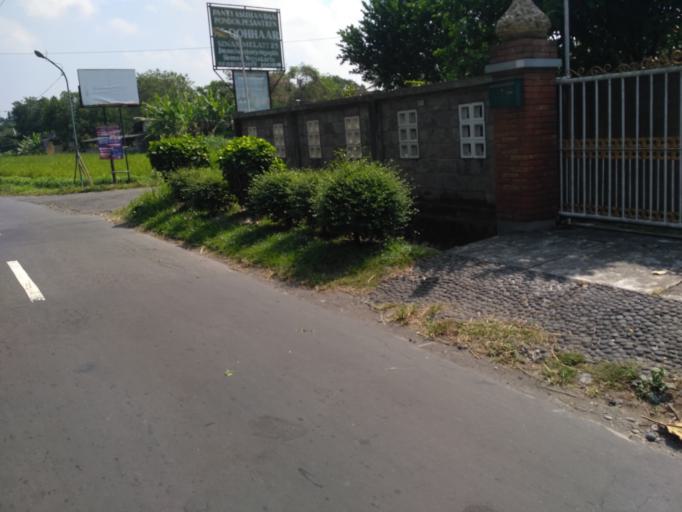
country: ID
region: Daerah Istimewa Yogyakarta
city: Depok
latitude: -7.7189
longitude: 110.4186
